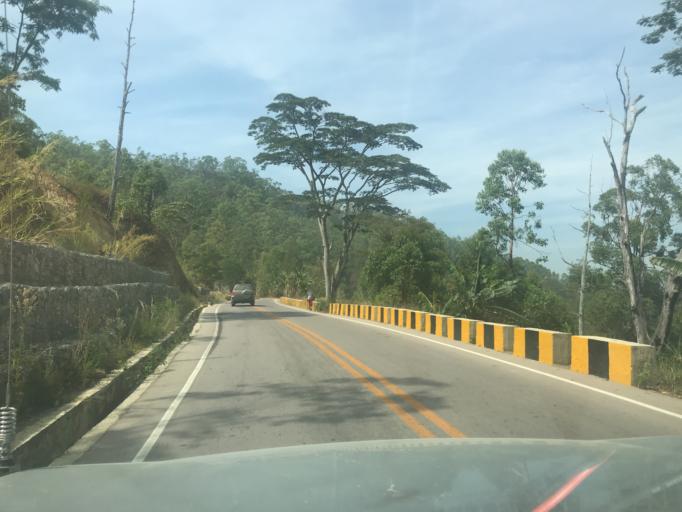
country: TL
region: Aileu
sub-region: Aileu Villa
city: Aileu
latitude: -8.6706
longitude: 125.5568
